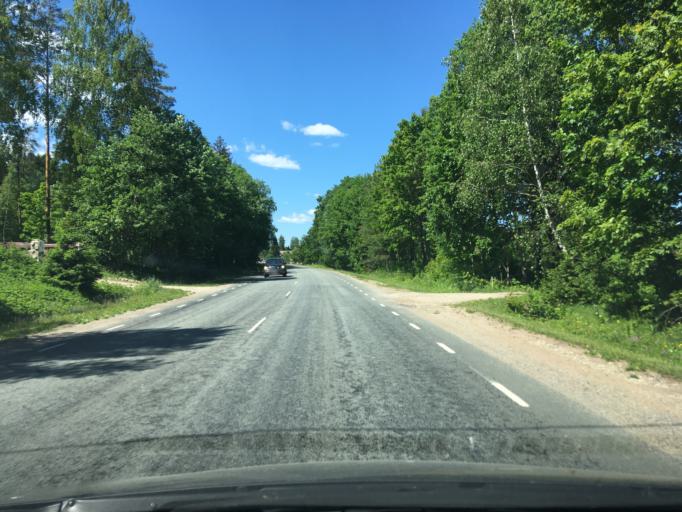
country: EE
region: Harju
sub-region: Rae vald
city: Vaida
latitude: 59.1964
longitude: 24.9834
